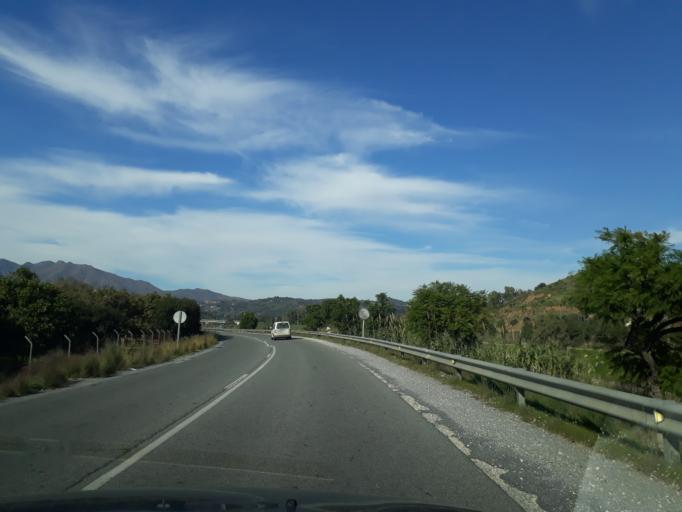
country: ES
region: Andalusia
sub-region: Provincia de Malaga
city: Fuengirola
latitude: 36.5462
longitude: -4.6890
